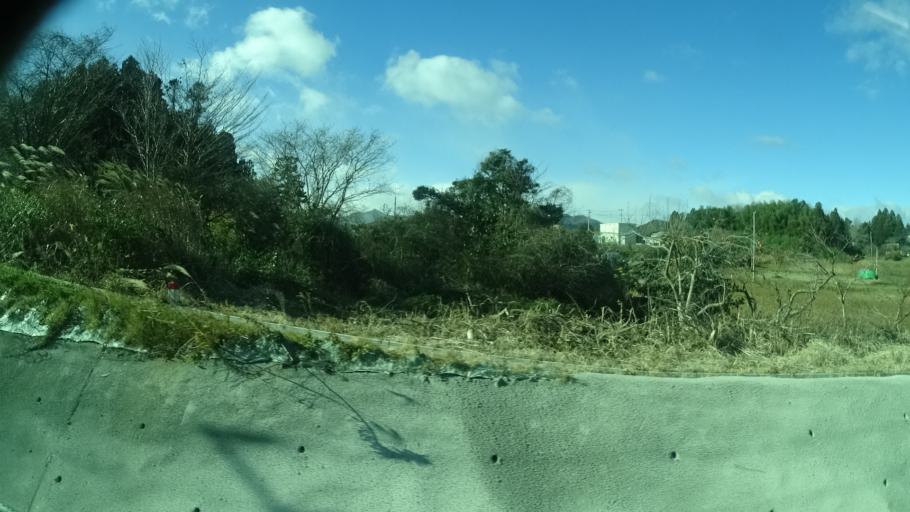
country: JP
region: Miyagi
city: Marumori
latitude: 37.8853
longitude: 140.9234
